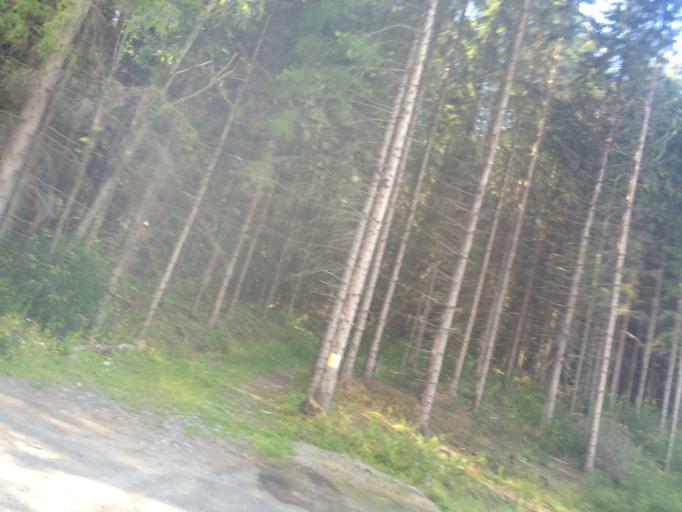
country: NO
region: Akershus
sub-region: As
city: As
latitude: 59.6785
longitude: 10.7591
